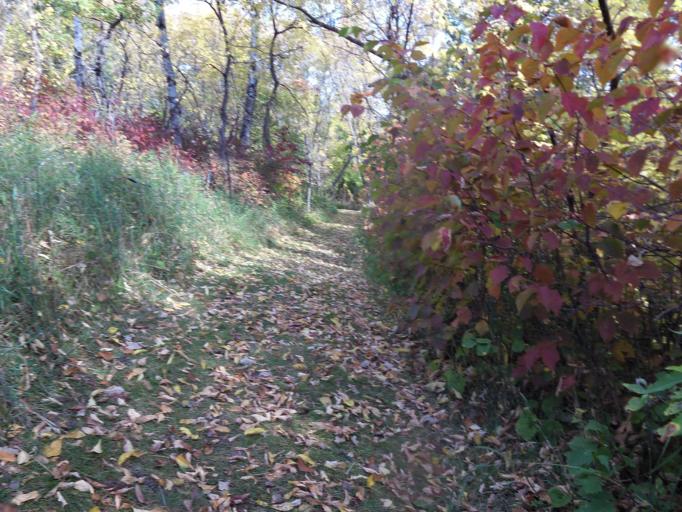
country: US
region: North Dakota
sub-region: Pembina County
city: Cavalier
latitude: 48.7793
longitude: -97.7434
